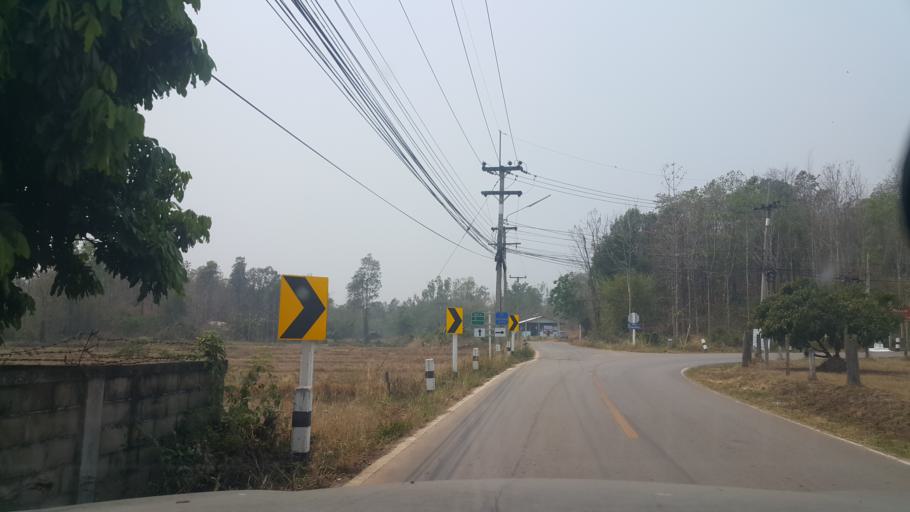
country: TH
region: Lampang
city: Soem Ngam
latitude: 18.1319
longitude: 99.1913
